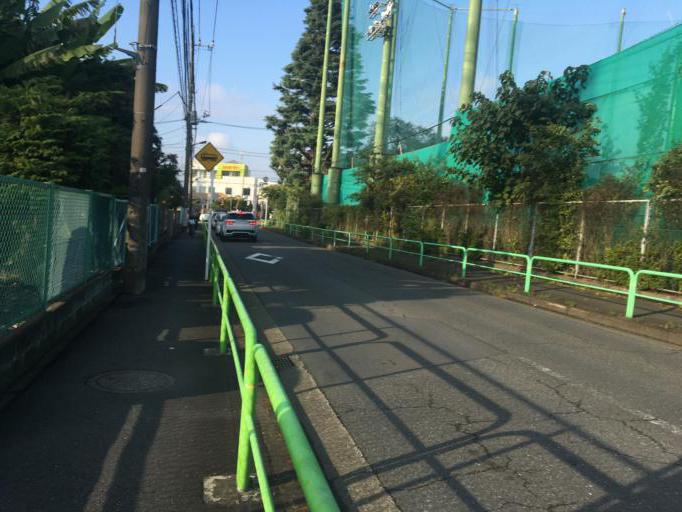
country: JP
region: Tokyo
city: Musashino
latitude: 35.7246
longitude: 139.5997
